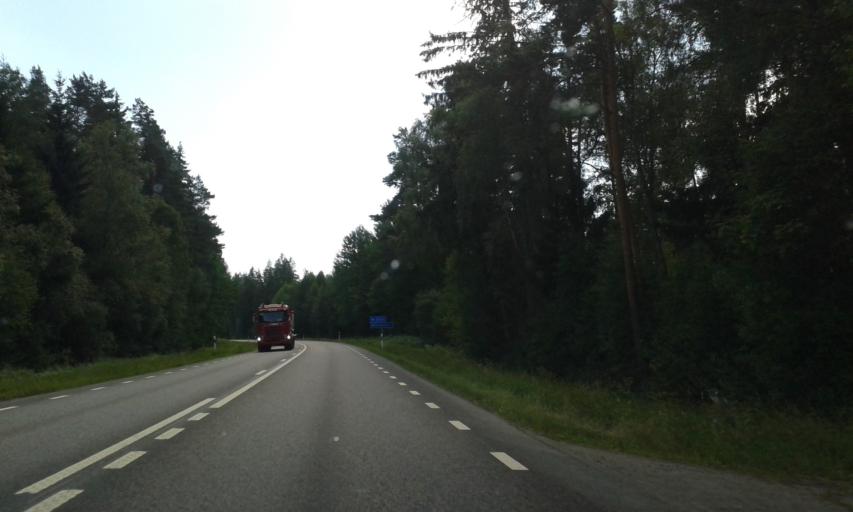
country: SE
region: Kronoberg
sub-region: Vaxjo Kommun
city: Ingelstad
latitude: 56.8164
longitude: 14.8808
